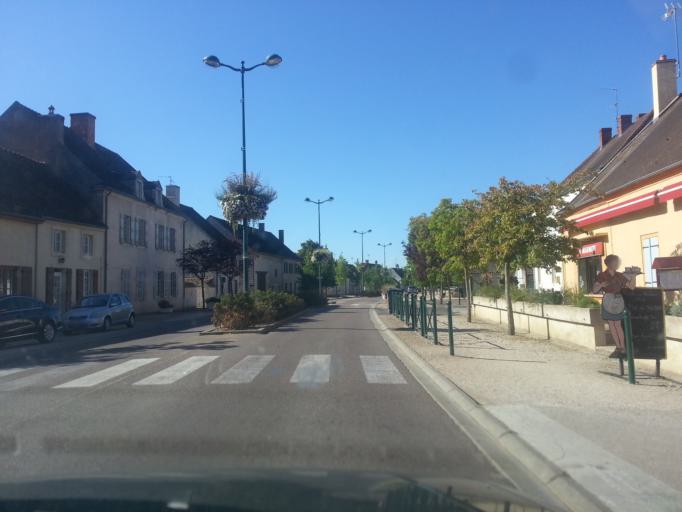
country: FR
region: Bourgogne
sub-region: Departement de Saone-et-Loire
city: Verdun-sur-le-Doubs
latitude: 46.8817
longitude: 5.0422
